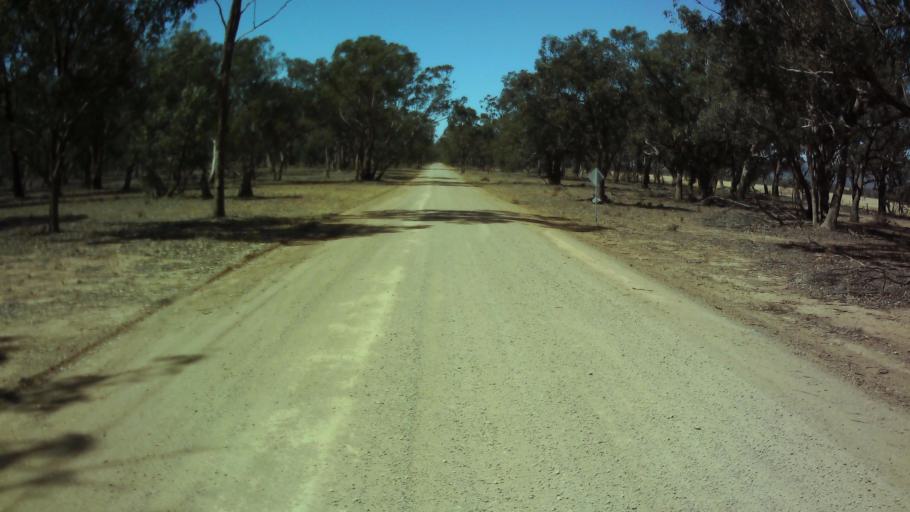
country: AU
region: New South Wales
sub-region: Weddin
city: Grenfell
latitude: -33.8505
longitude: 148.0884
